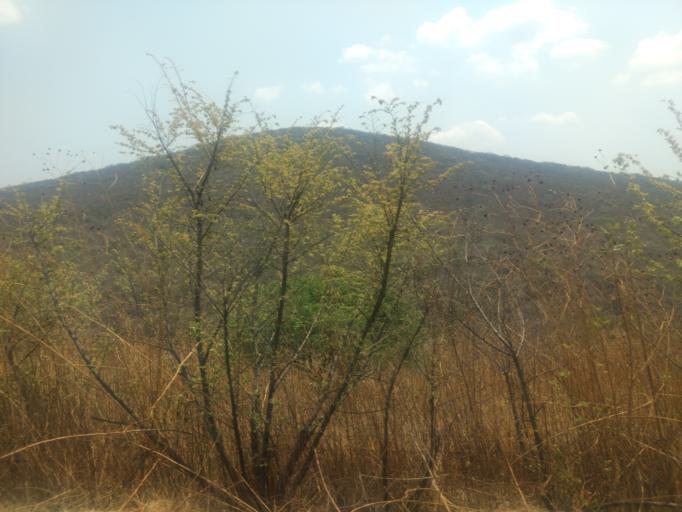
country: MX
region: Morelos
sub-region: Mazatepec
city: Cuauchichinola
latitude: 18.6537
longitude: -99.4051
